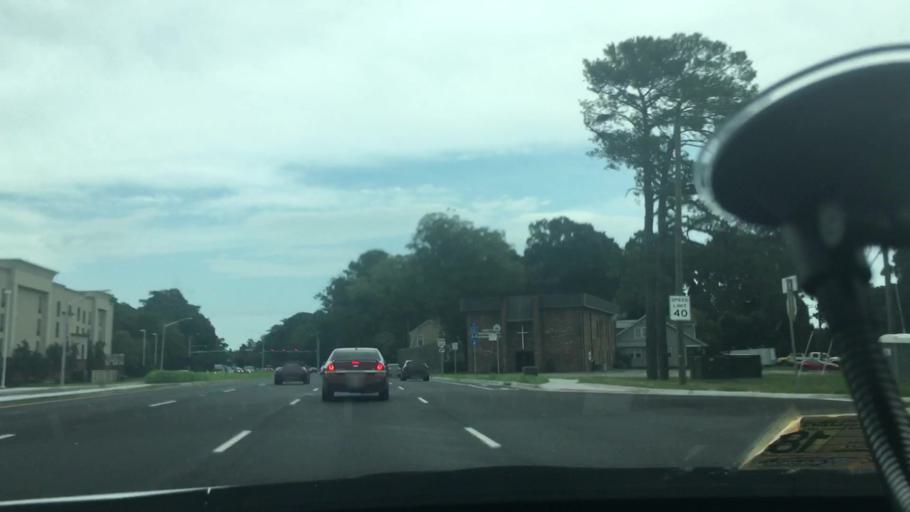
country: US
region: Virginia
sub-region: City of Norfolk
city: Norfolk
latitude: 36.8745
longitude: -76.2093
